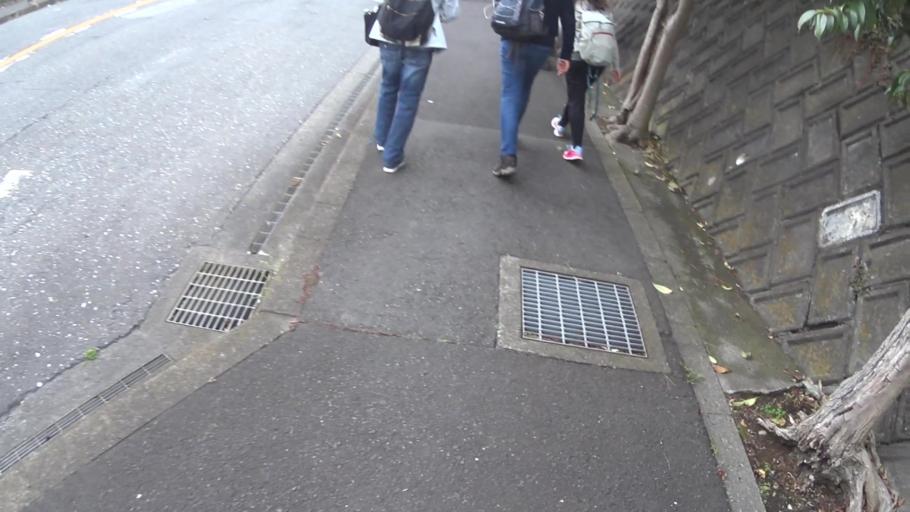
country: JP
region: Kanagawa
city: Fujisawa
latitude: 35.3171
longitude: 139.4985
